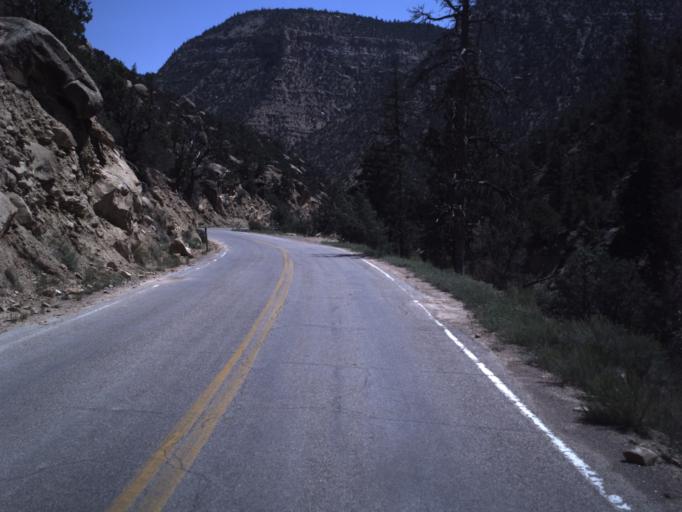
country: US
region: Utah
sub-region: Emery County
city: Orangeville
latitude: 39.2801
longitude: -111.2296
